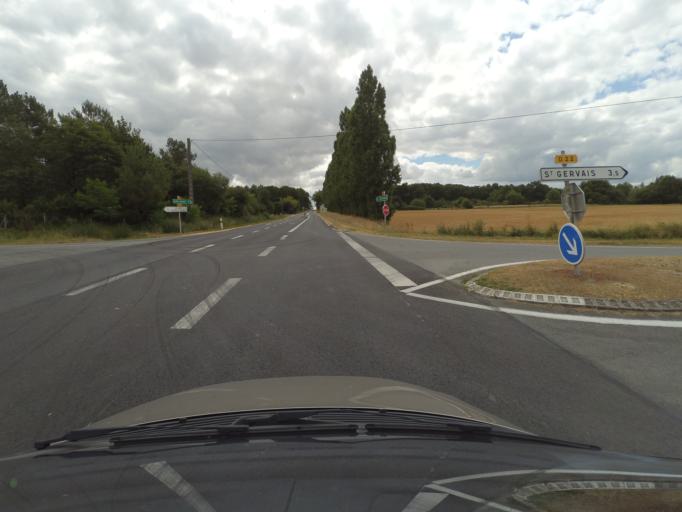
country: FR
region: Poitou-Charentes
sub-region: Departement de la Vienne
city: Saint-Gervais-les-Trois-Clochers
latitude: 46.9090
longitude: 0.4489
